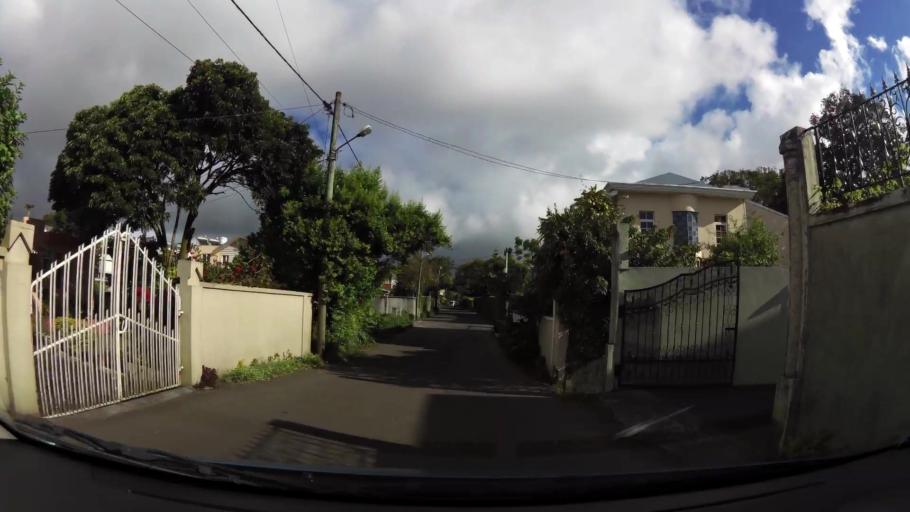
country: MU
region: Plaines Wilhems
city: Curepipe
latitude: -20.3250
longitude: 57.5188
